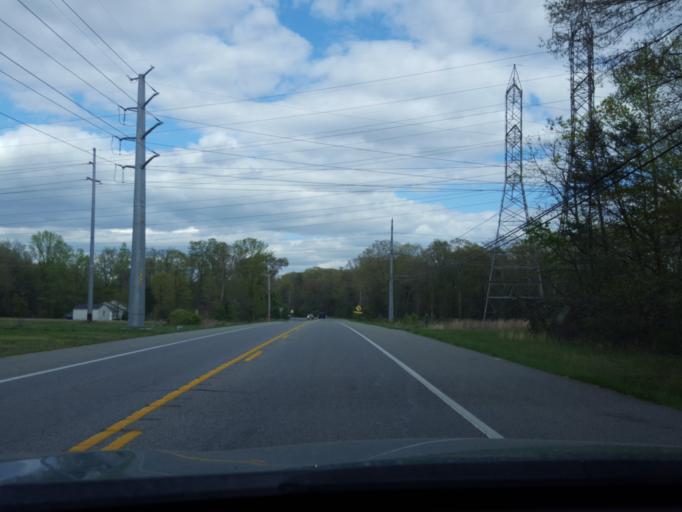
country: US
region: Maryland
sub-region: Charles County
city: Saint Charles
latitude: 38.5450
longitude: -76.9132
